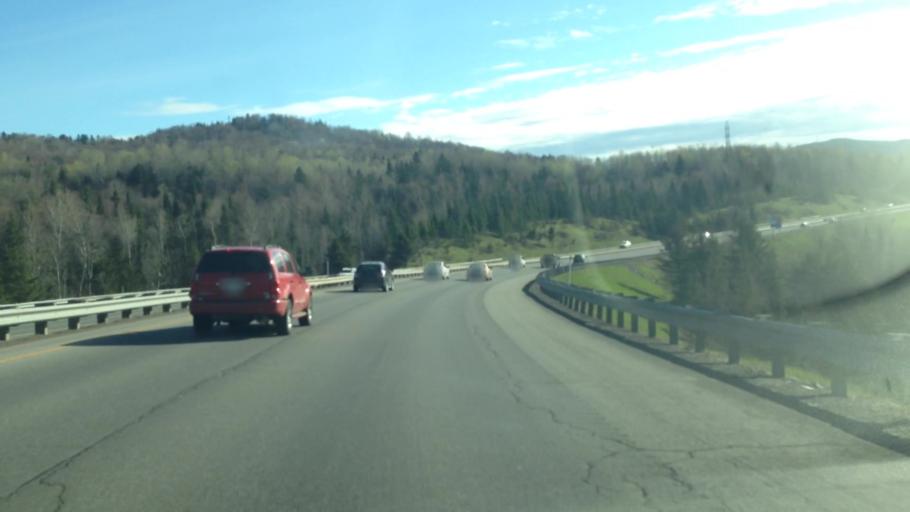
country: CA
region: Quebec
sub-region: Laurentides
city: Sainte-Adele
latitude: 45.9332
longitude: -74.1444
